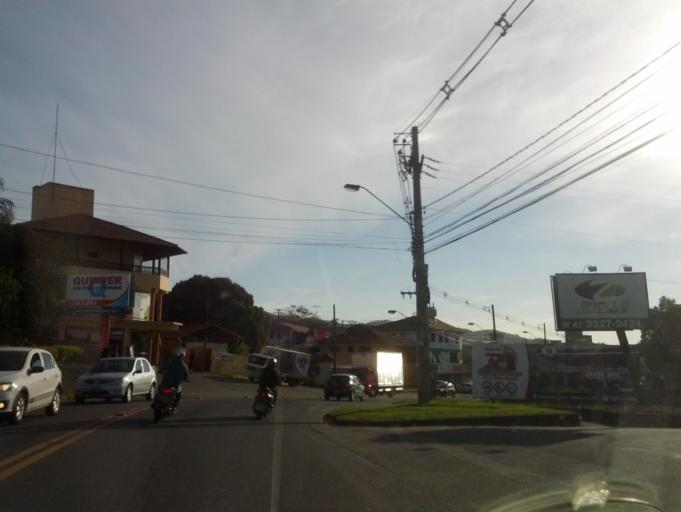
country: BR
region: Santa Catarina
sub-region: Blumenau
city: Blumenau
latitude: -26.9111
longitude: -49.1155
